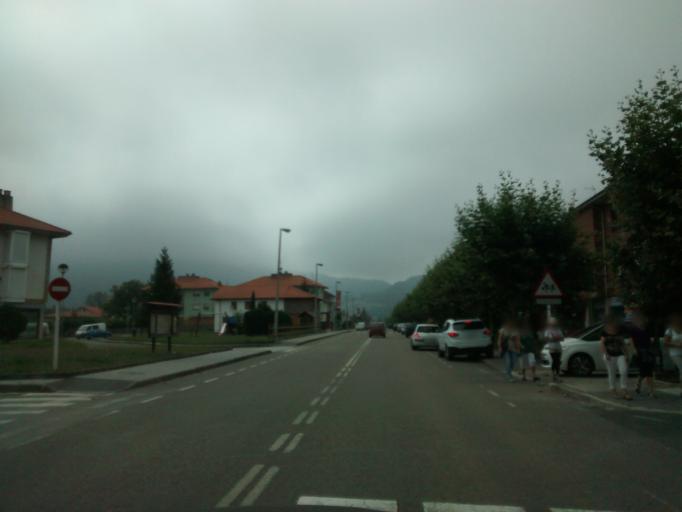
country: ES
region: Cantabria
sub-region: Provincia de Cantabria
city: Cabezon de la Sal
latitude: 43.3028
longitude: -4.2378
